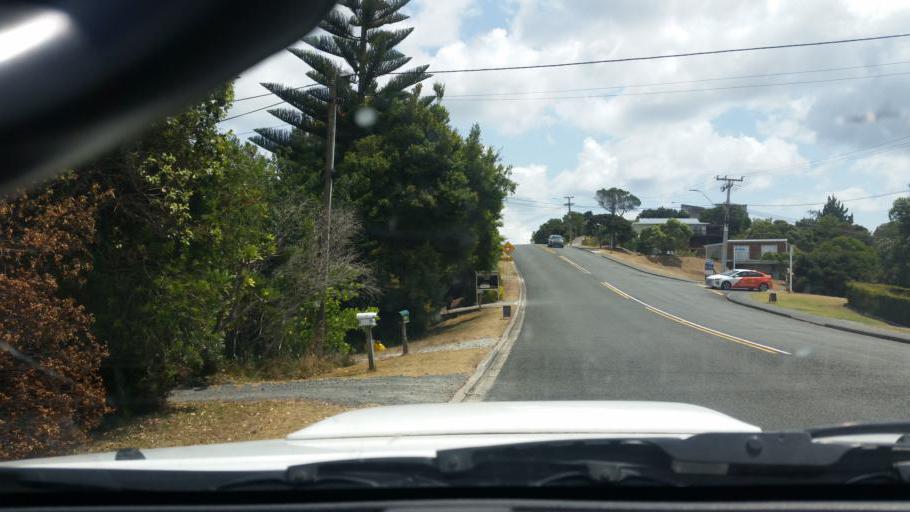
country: NZ
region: Auckland
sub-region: Auckland
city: Wellsford
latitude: -36.0891
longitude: 174.5838
